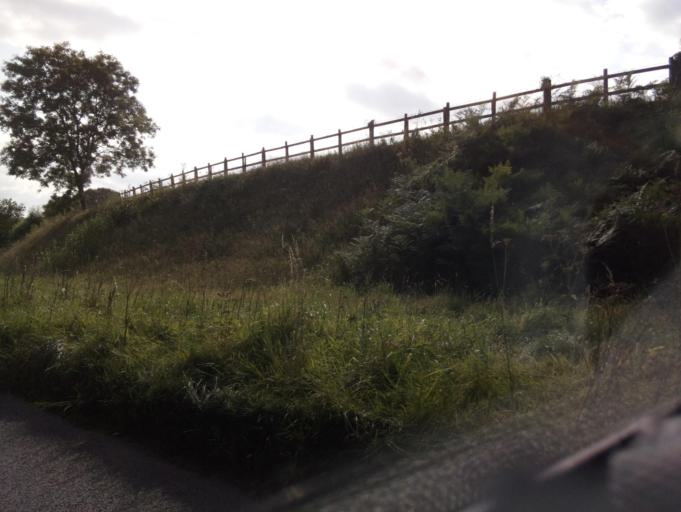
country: GB
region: England
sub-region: Devon
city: Tiverton
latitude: 50.8632
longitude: -3.5056
